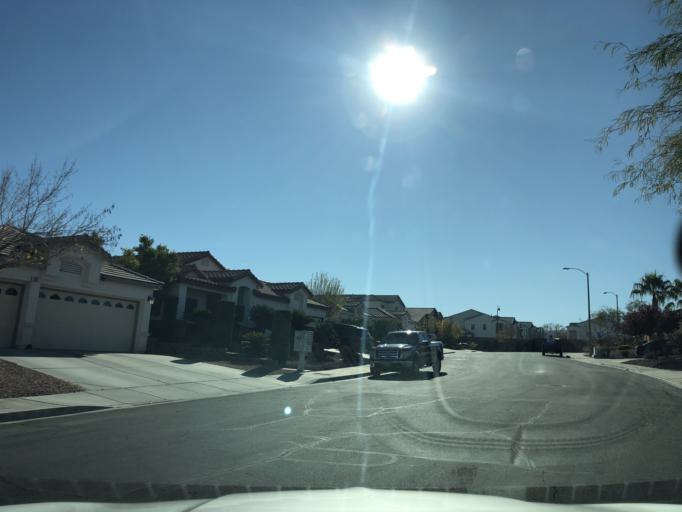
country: US
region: Nevada
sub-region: Clark County
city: Whitney
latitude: 36.0096
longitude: -115.0854
